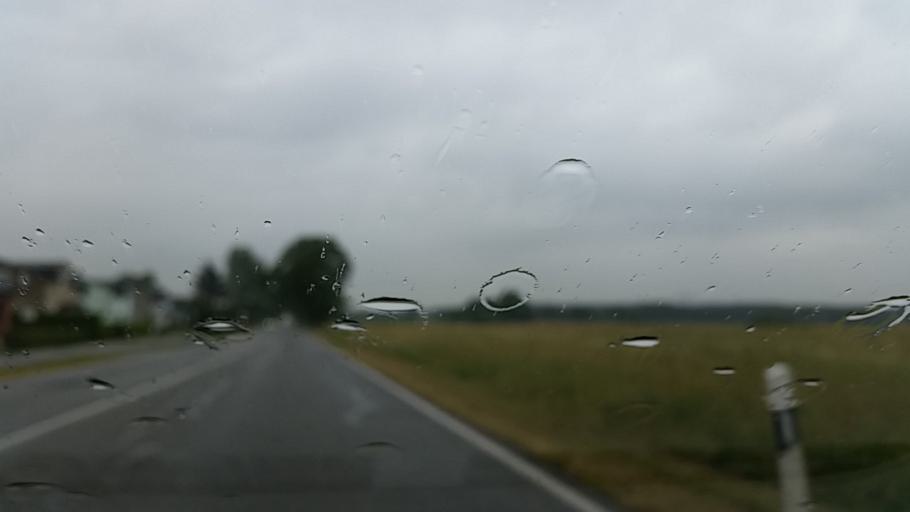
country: DE
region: Mecklenburg-Vorpommern
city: Biendorf
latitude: 54.0496
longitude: 11.7257
